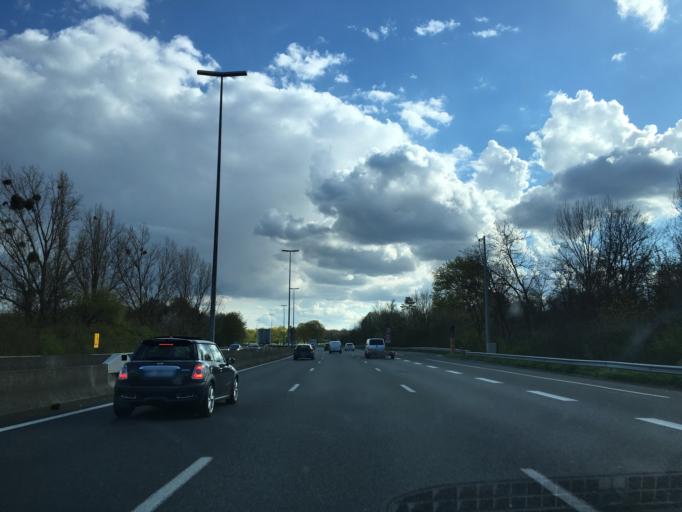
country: FR
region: Picardie
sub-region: Departement de l'Oise
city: Senlis
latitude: 49.1975
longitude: 2.6050
